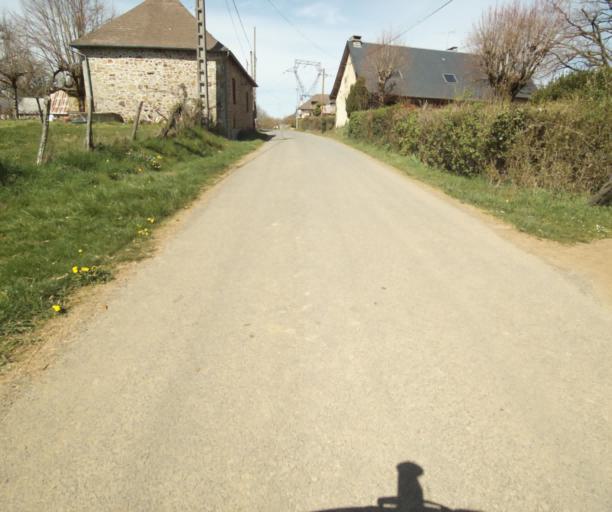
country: FR
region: Limousin
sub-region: Departement de la Correze
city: Seilhac
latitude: 45.4006
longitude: 1.7866
